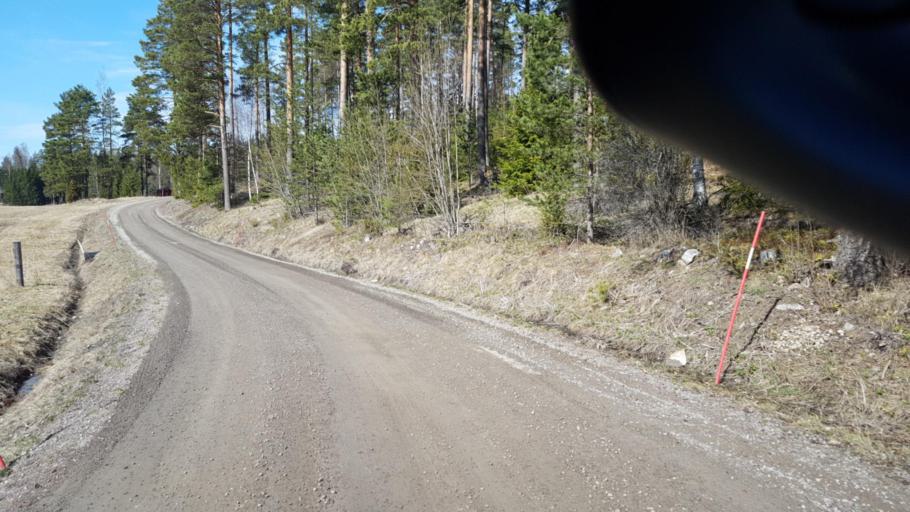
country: SE
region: Vaermland
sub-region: Grums Kommun
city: Grums
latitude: 59.5103
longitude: 12.9281
